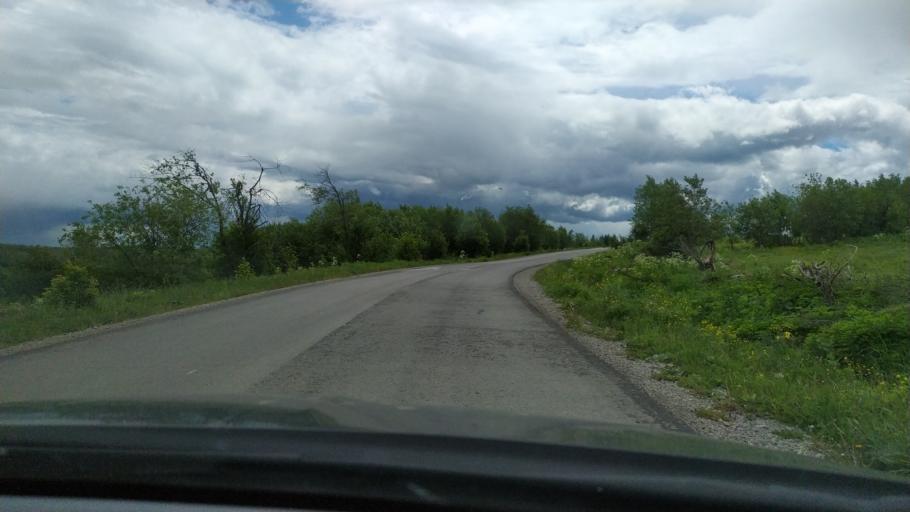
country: RU
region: Perm
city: Gremyachinsk
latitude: 58.5337
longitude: 57.8289
